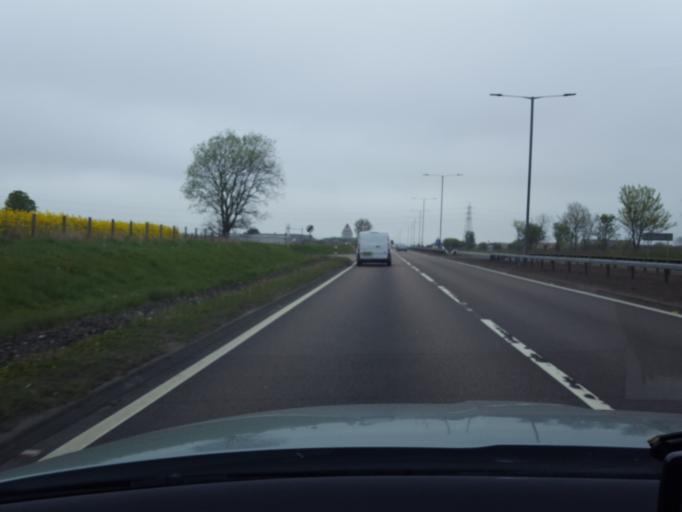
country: GB
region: Scotland
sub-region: Dundee City
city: Dundee
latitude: 56.5160
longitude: -2.9452
